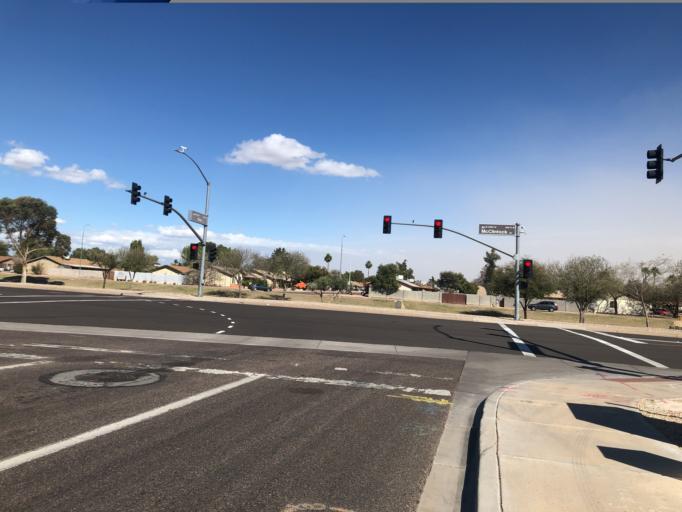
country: US
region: Arizona
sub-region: Maricopa County
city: Chandler
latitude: 33.3089
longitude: -111.9115
